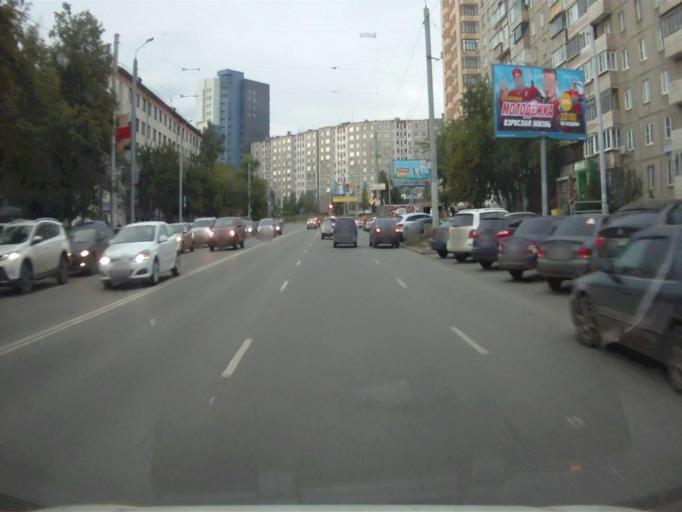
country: RU
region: Chelyabinsk
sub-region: Gorod Chelyabinsk
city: Chelyabinsk
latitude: 55.1547
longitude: 61.3815
